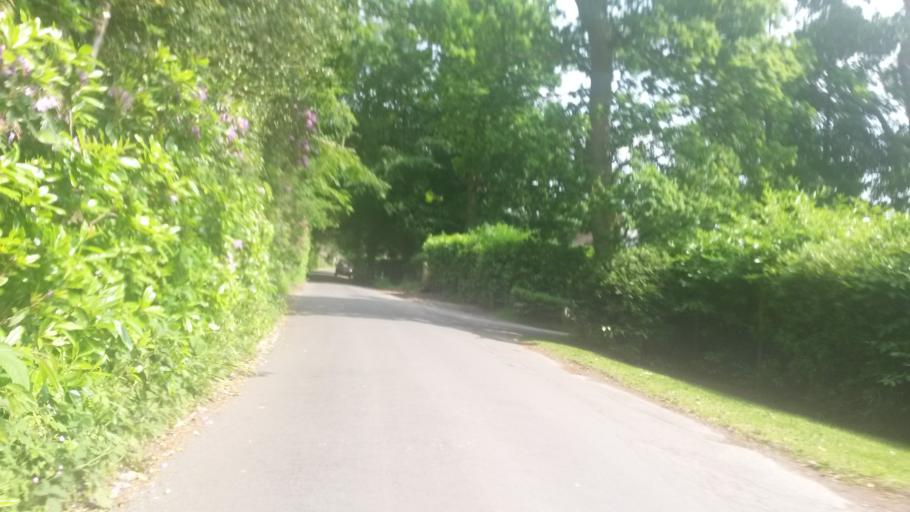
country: GB
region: England
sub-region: Surrey
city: Haslemere
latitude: 51.0783
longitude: -0.6999
